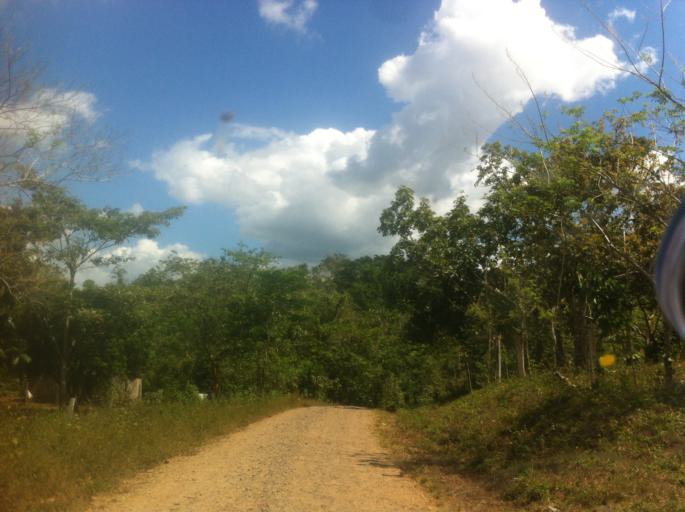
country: CR
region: Alajuela
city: Los Chiles
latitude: 11.2340
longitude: -84.4957
